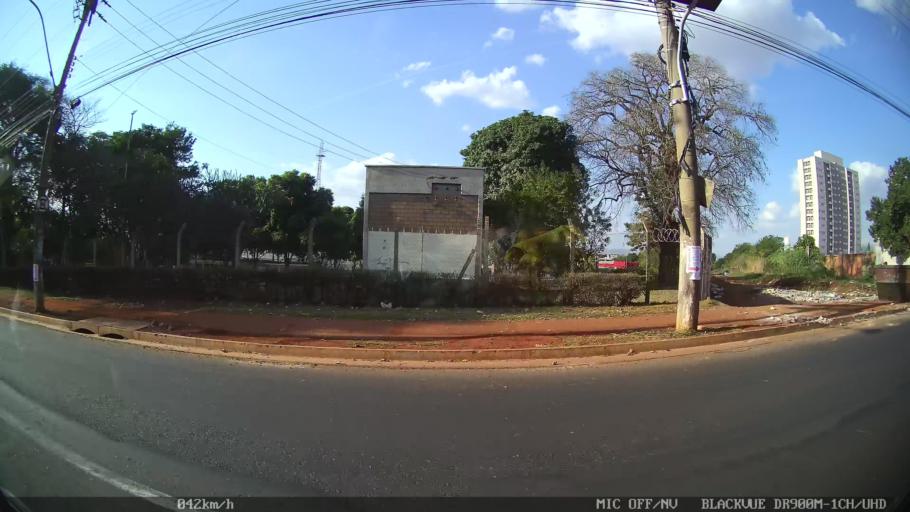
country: BR
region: Sao Paulo
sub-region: Ribeirao Preto
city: Ribeirao Preto
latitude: -21.1481
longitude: -47.8293
